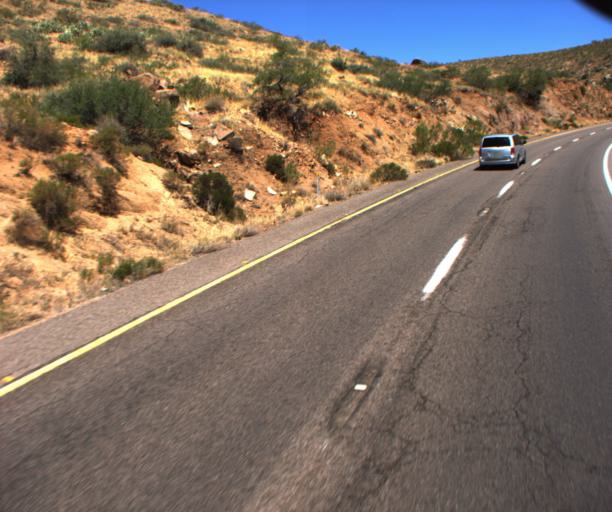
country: US
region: Arizona
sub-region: Gila County
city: Tonto Basin
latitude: 33.8348
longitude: -111.4733
